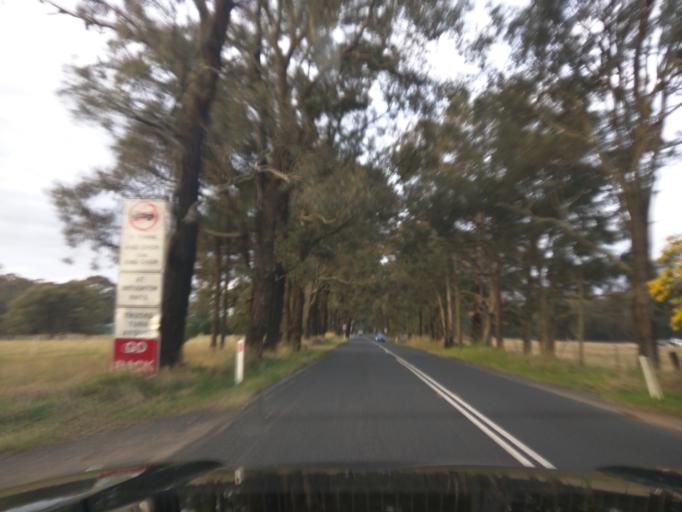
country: AU
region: New South Wales
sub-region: Wollondilly
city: Douglas Park
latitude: -34.2344
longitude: 150.7333
